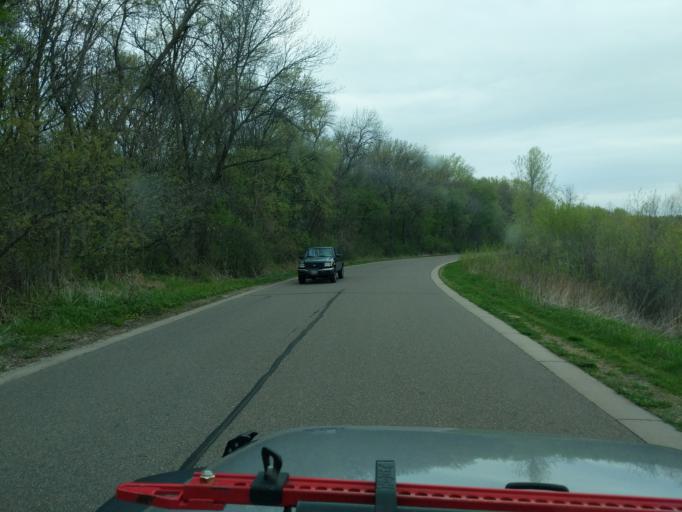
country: US
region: Minnesota
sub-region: Anoka County
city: Coon Rapids
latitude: 45.1421
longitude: -93.2988
